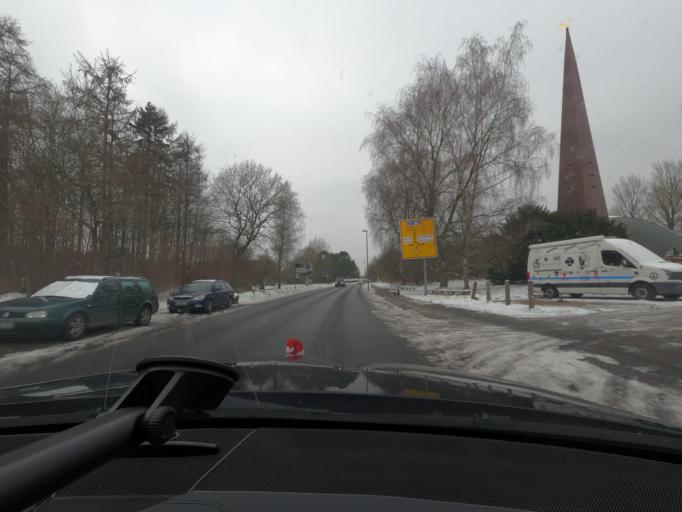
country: DE
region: Schleswig-Holstein
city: Jarplund-Weding
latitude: 54.7636
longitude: 9.3953
